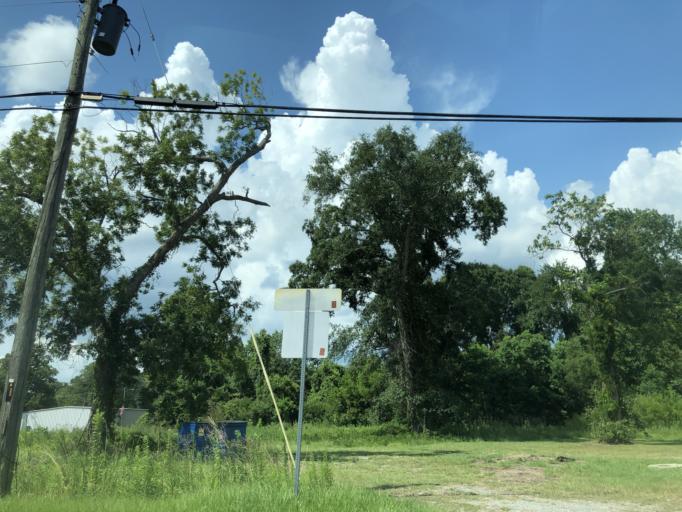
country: US
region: Georgia
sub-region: Telfair County
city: McRae
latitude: 32.0654
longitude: -82.8922
